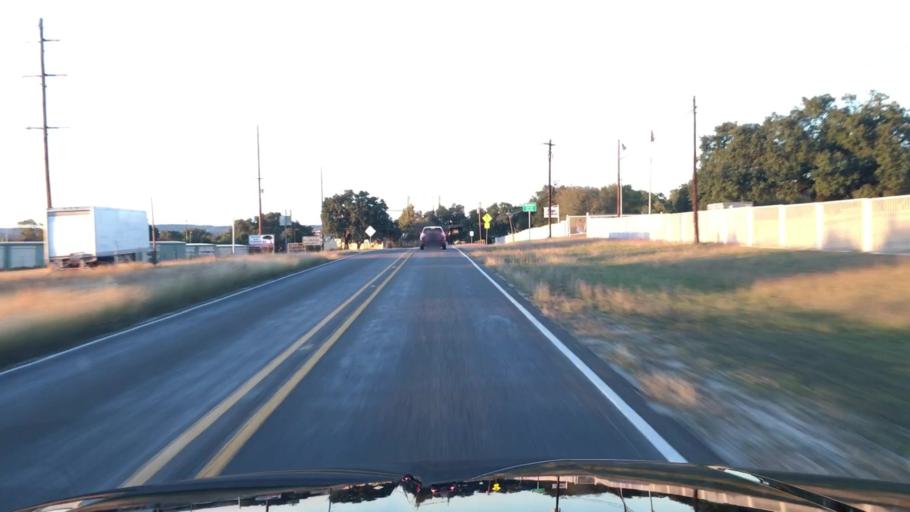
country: US
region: Texas
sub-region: Blanco County
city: Blanco
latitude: 30.0798
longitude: -98.4120
